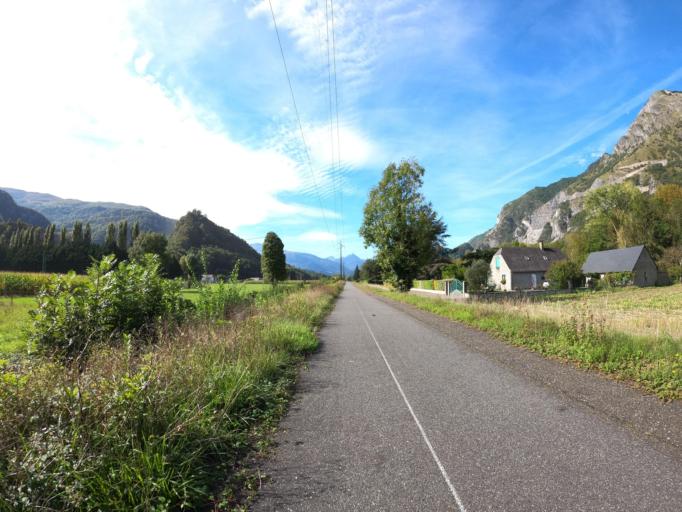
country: FR
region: Midi-Pyrenees
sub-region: Departement des Hautes-Pyrenees
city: Lourdes
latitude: 43.0504
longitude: -0.0479
